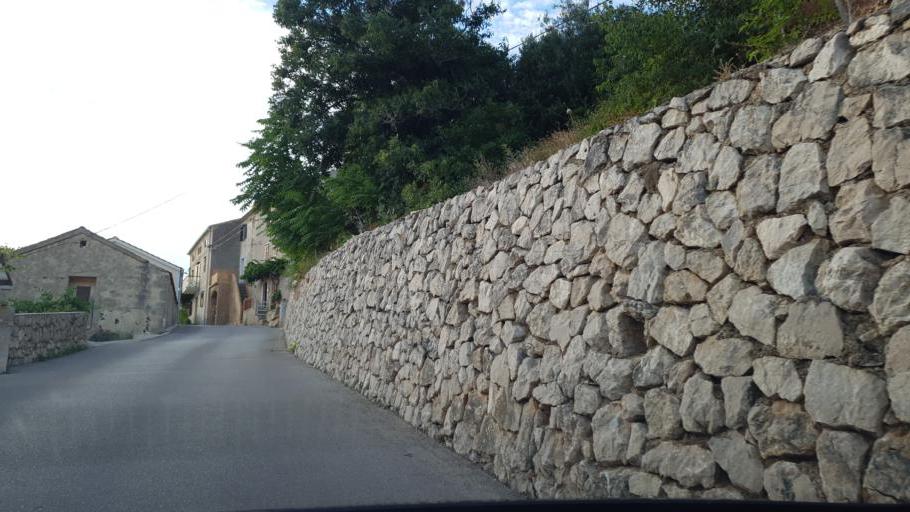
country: HR
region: Primorsko-Goranska
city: Punat
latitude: 44.9582
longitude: 14.6885
